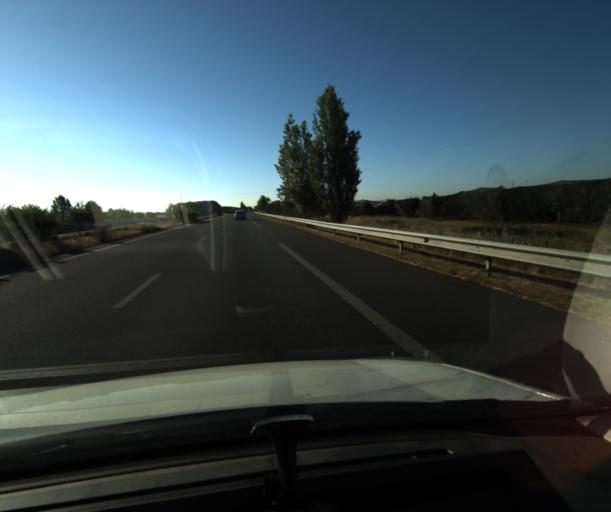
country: FR
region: Midi-Pyrenees
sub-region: Departement du Tarn-et-Garonne
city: Castelsarrasin
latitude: 44.0481
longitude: 1.1408
